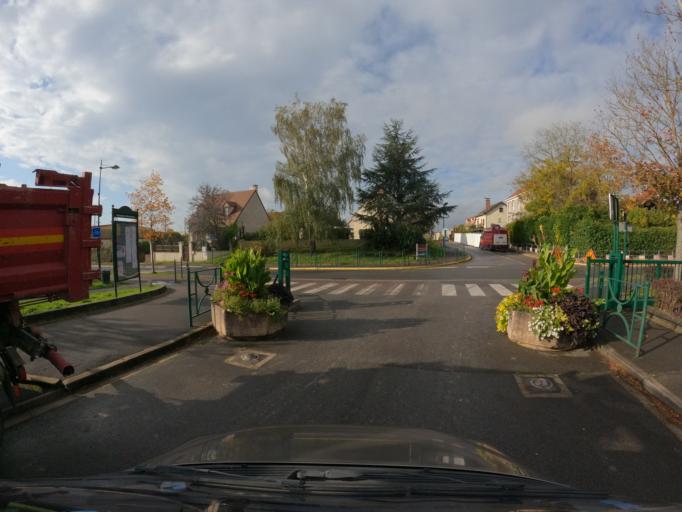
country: FR
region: Ile-de-France
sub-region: Departement de Seine-et-Marne
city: Courtry
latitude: 48.9166
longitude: 2.6036
